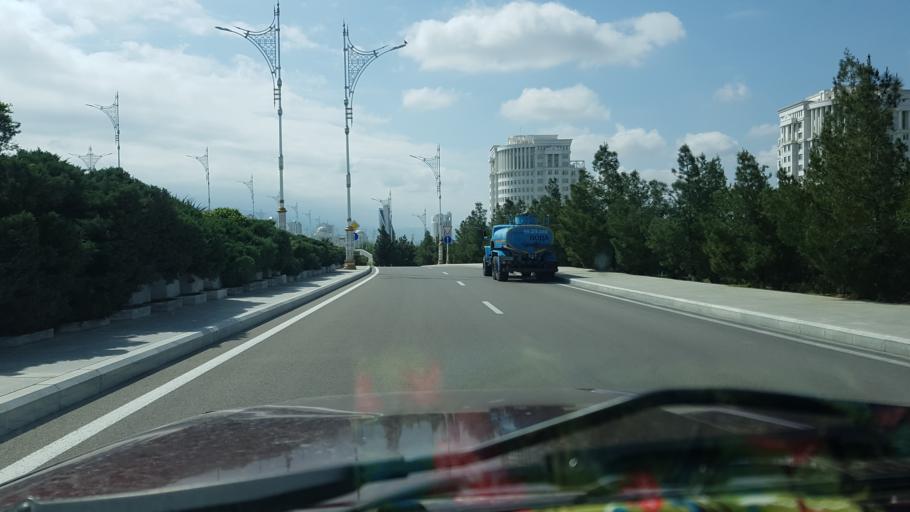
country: TM
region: Ahal
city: Ashgabat
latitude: 37.8795
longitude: 58.3800
